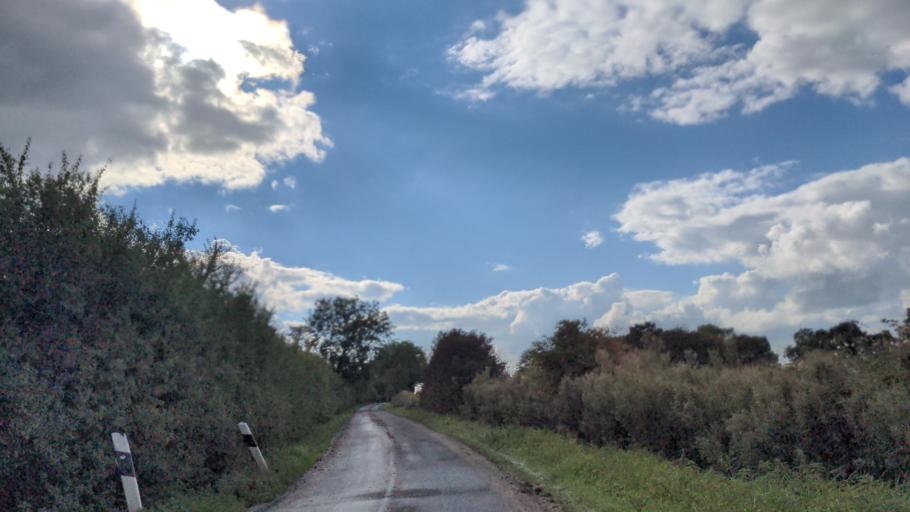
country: DE
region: Schleswig-Holstein
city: Stockelsdorf
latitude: 53.9238
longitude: 10.6182
